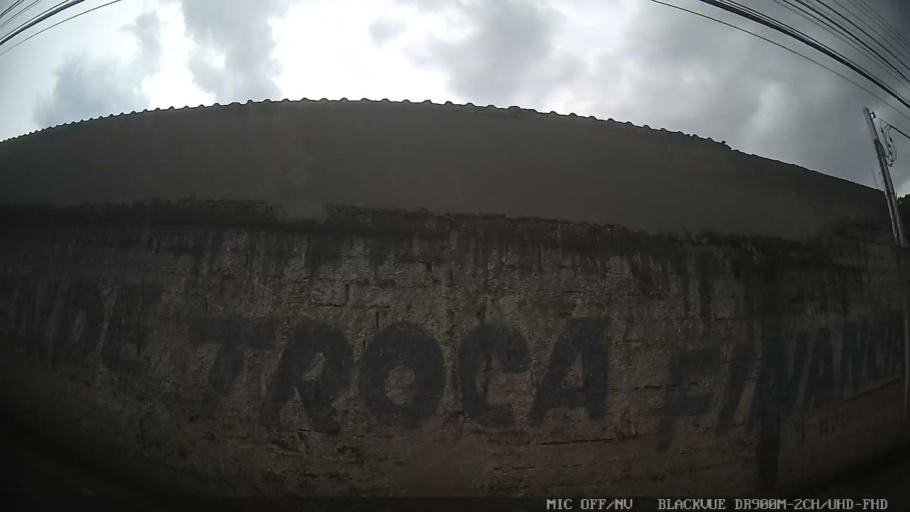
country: BR
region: Sao Paulo
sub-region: Suzano
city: Suzano
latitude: -23.5561
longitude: -46.3092
